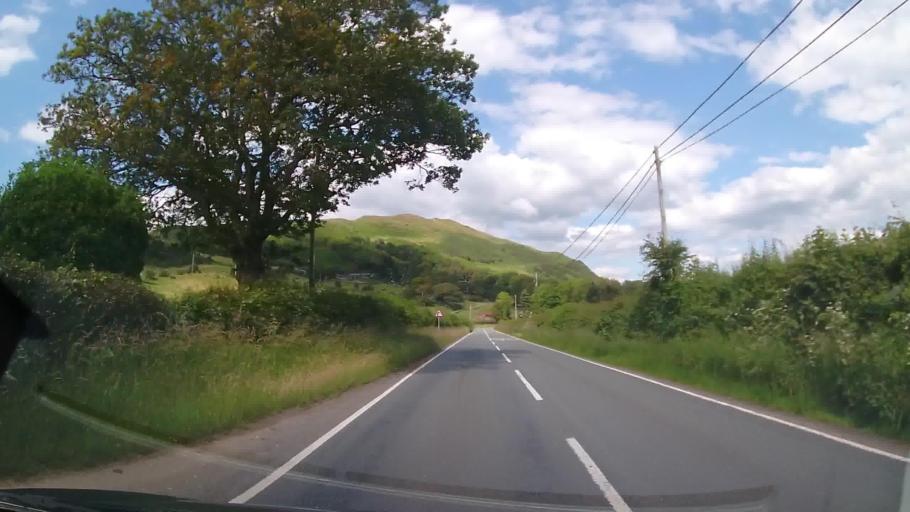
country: GB
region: Wales
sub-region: Gwynedd
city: Tywyn
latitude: 52.6089
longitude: -4.0469
